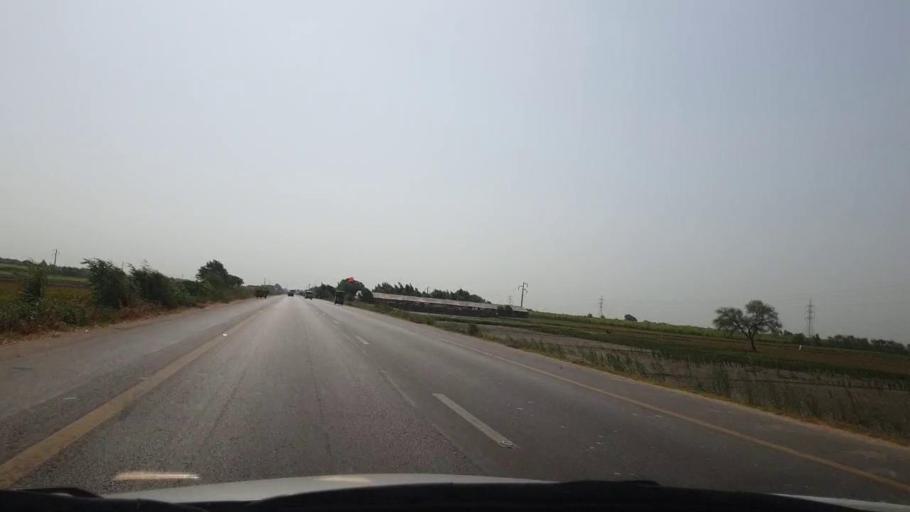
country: PK
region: Sindh
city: Tando Muhammad Khan
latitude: 25.1172
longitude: 68.5740
